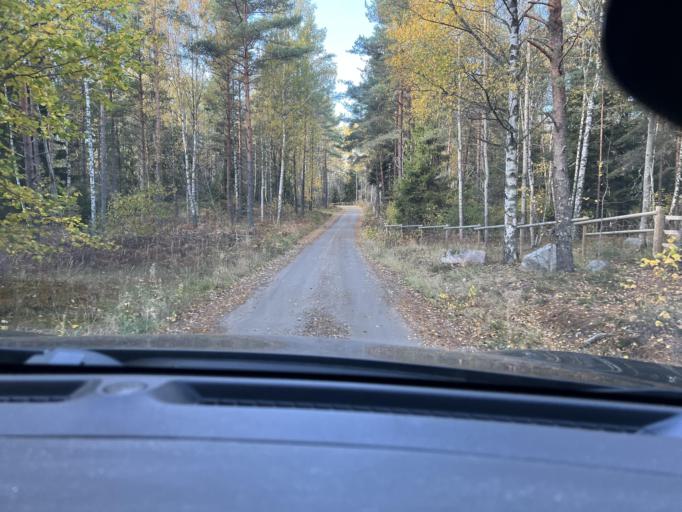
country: SE
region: Stockholm
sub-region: Vallentuna Kommun
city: Vallentuna
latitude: 59.5102
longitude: 18.1242
